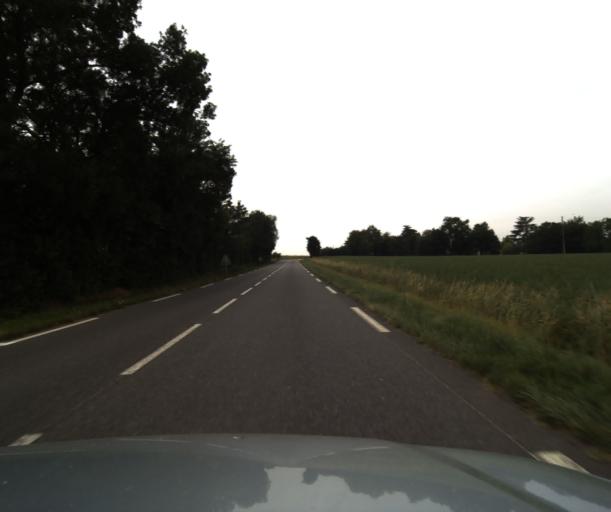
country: FR
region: Midi-Pyrenees
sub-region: Departement du Gers
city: Aubiet
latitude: 43.6721
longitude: 0.8051
